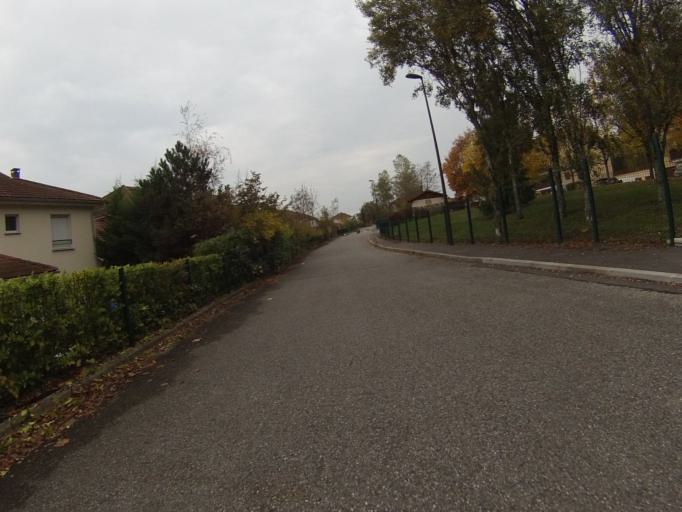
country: CH
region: Geneva
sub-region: Geneva
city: Meyrin
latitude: 46.2513
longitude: 6.0836
